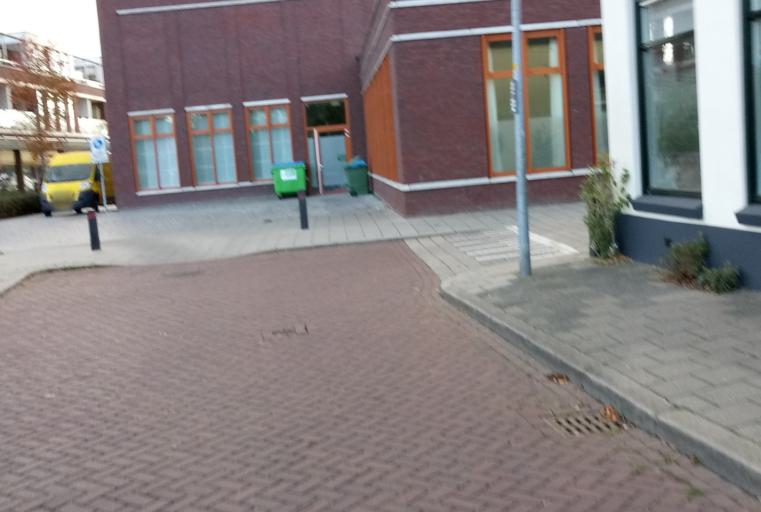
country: NL
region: Gelderland
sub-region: Gemeente Zutphen
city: Zutphen
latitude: 52.1342
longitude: 6.2047
